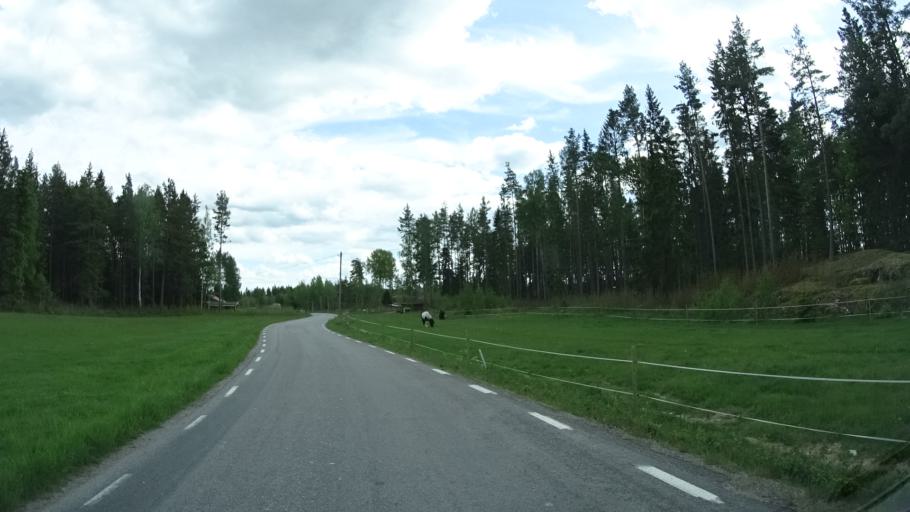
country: SE
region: OEstergoetland
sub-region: Finspangs Kommun
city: Finspang
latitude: 58.6028
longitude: 15.7569
